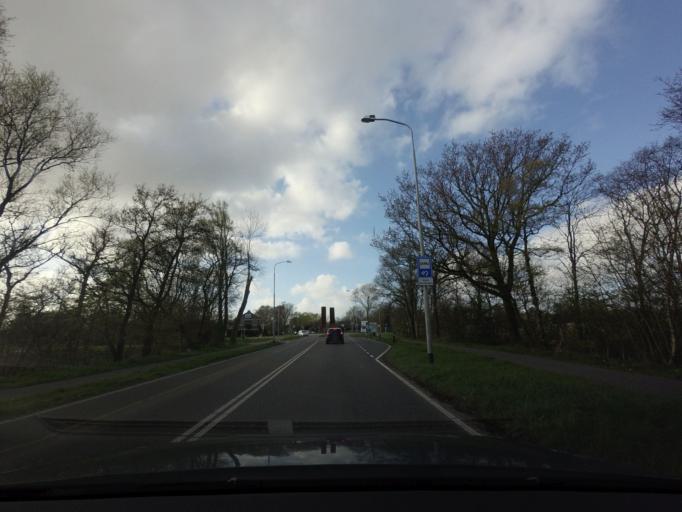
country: NL
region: North Holland
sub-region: Gemeente Alkmaar
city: Alkmaar
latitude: 52.6598
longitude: 4.7165
